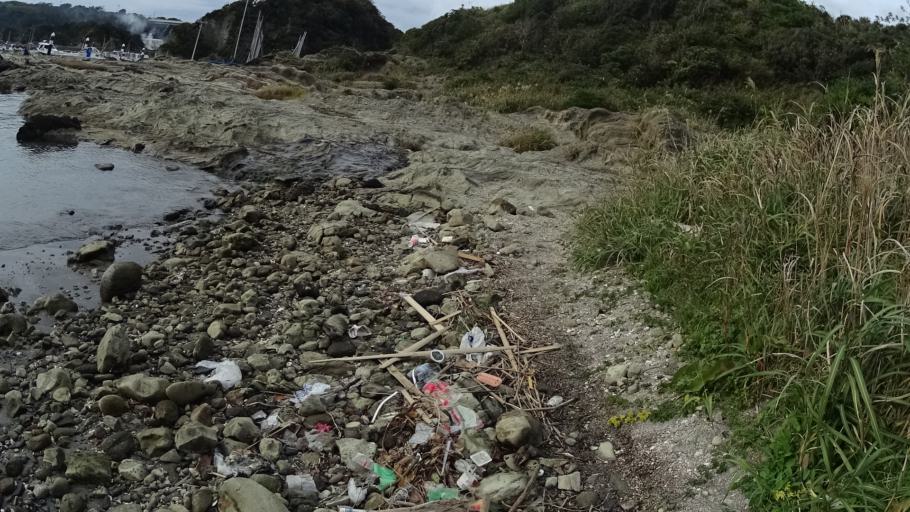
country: JP
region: Kanagawa
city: Miura
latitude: 35.1398
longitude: 139.6406
